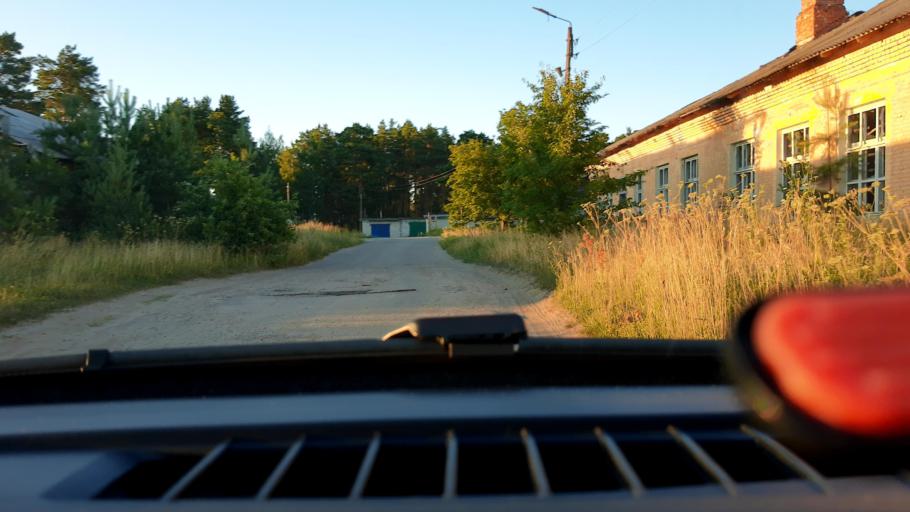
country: RU
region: Nizjnij Novgorod
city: Lukino
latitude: 56.3918
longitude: 43.7200
